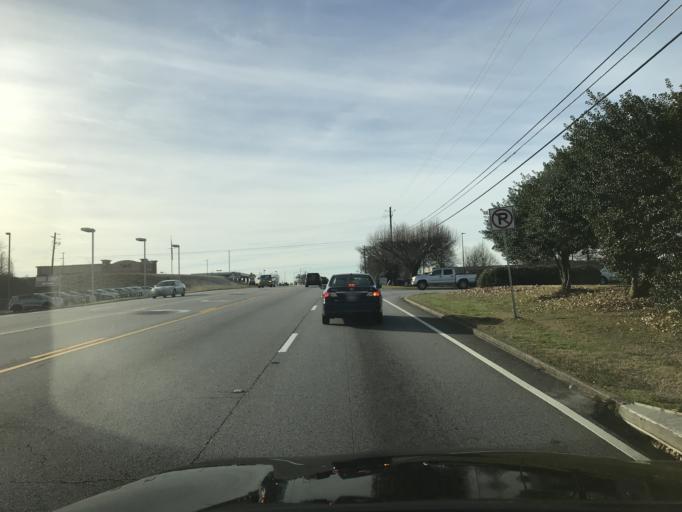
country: US
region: Georgia
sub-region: Clayton County
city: Morrow
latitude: 33.5563
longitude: -84.3466
